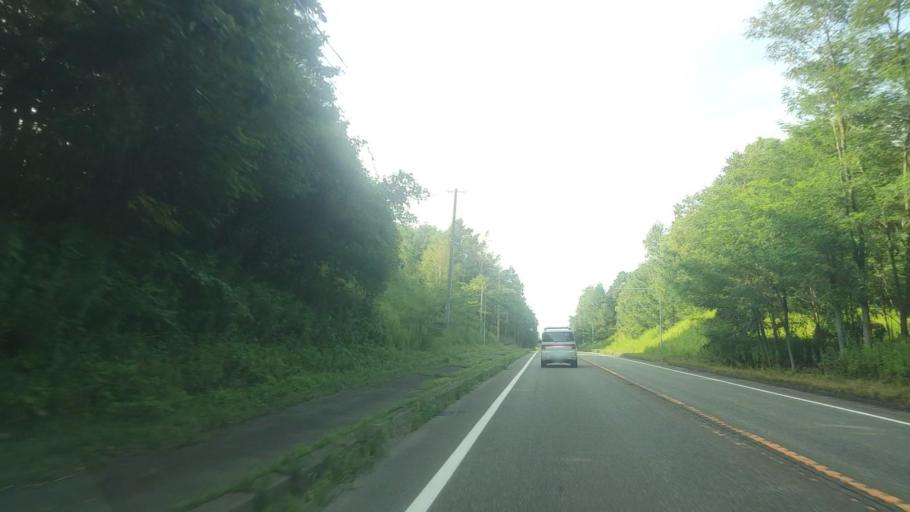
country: JP
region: Hokkaido
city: Chitose
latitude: 42.8696
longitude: 141.8226
